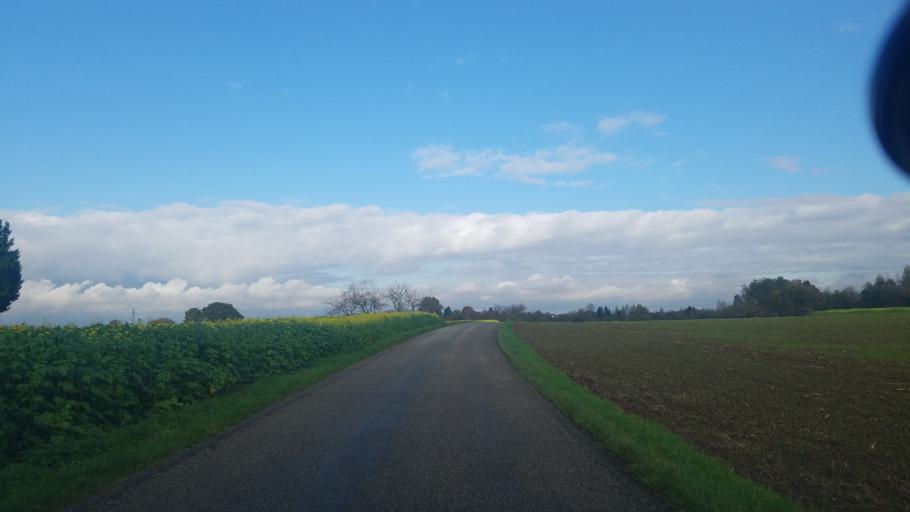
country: DE
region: Baden-Wuerttemberg
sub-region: Karlsruhe Region
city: Lichtenau
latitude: 48.6851
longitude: 7.9868
